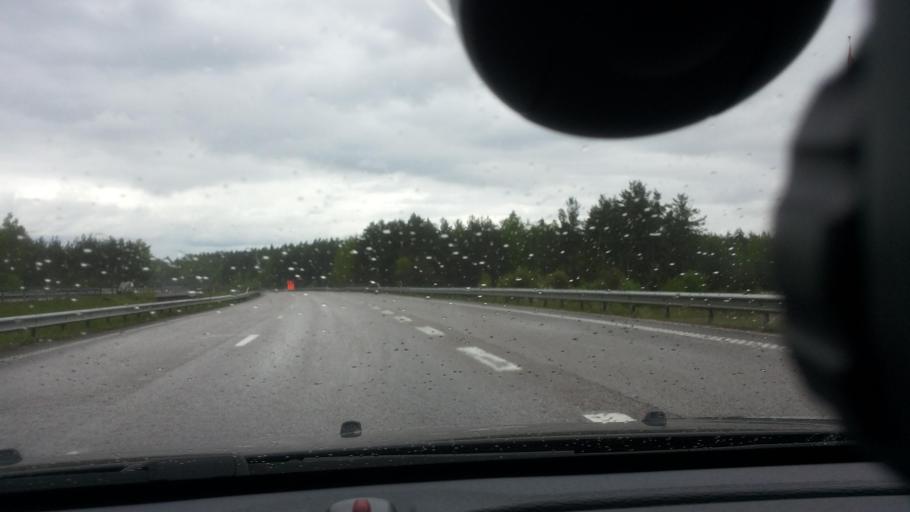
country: SE
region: Uppsala
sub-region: Alvkarleby Kommun
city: AElvkarleby
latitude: 60.4622
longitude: 17.4136
